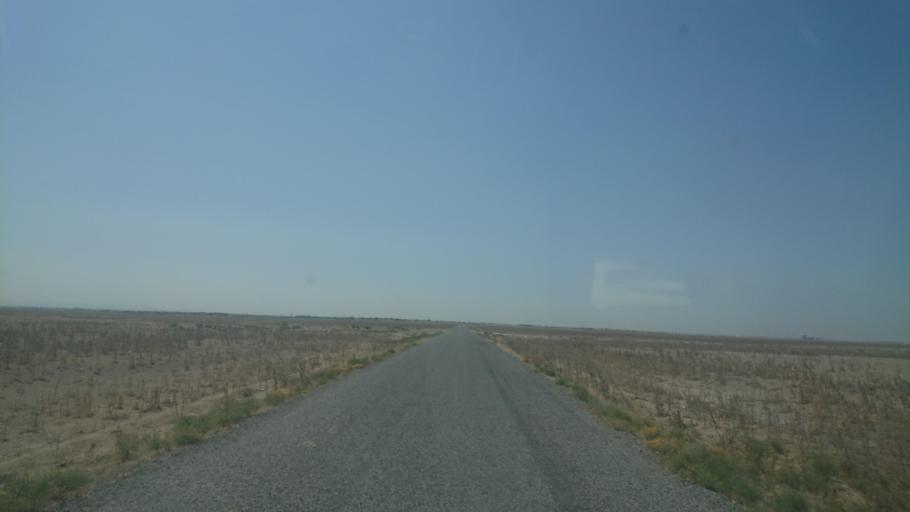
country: TR
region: Aksaray
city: Yesilova
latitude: 38.3129
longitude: 33.7386
